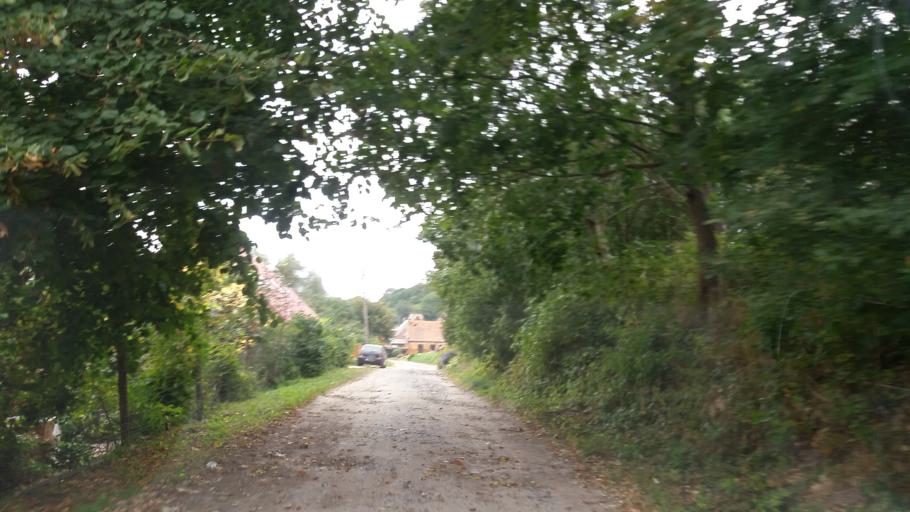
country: PL
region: West Pomeranian Voivodeship
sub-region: Powiat choszczenski
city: Bierzwnik
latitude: 52.9988
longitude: 15.5995
